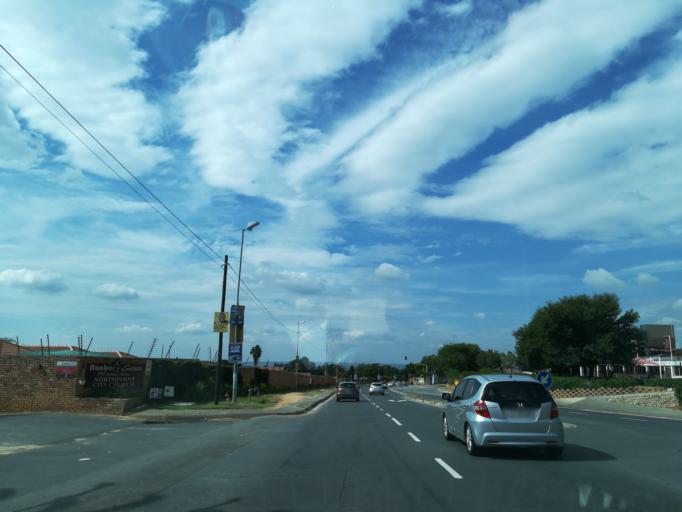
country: ZA
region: Gauteng
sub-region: West Rand District Municipality
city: Muldersdriseloop
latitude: -26.0597
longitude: 27.9568
